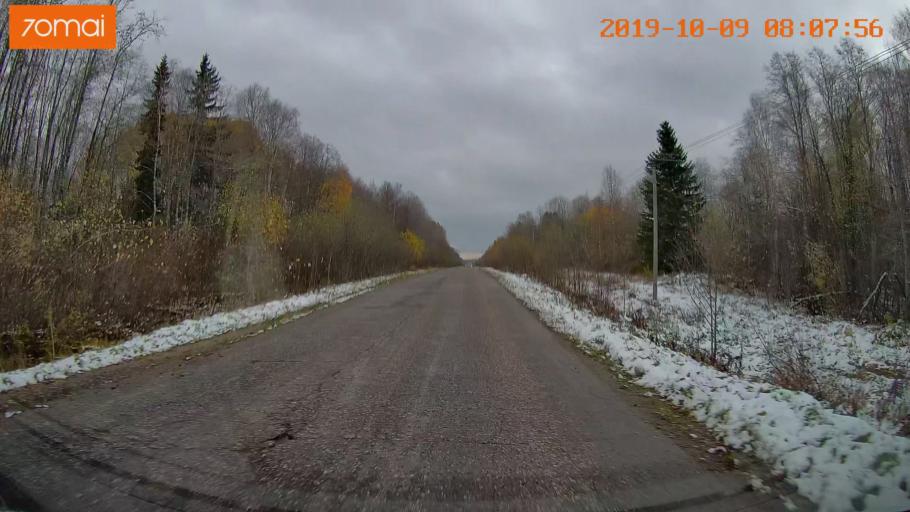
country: RU
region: Jaroslavl
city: Kukoboy
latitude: 58.7009
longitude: 40.0878
